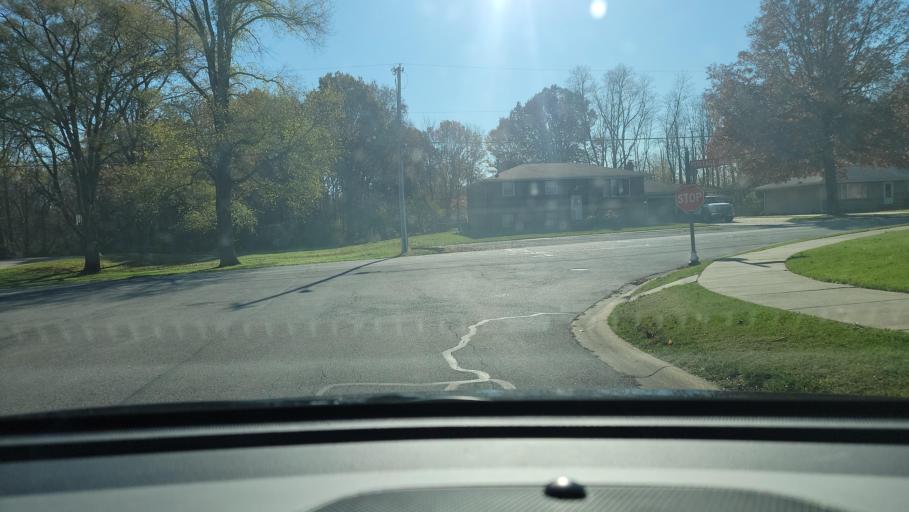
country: US
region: Indiana
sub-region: Porter County
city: Portage
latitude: 41.5869
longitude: -87.1476
